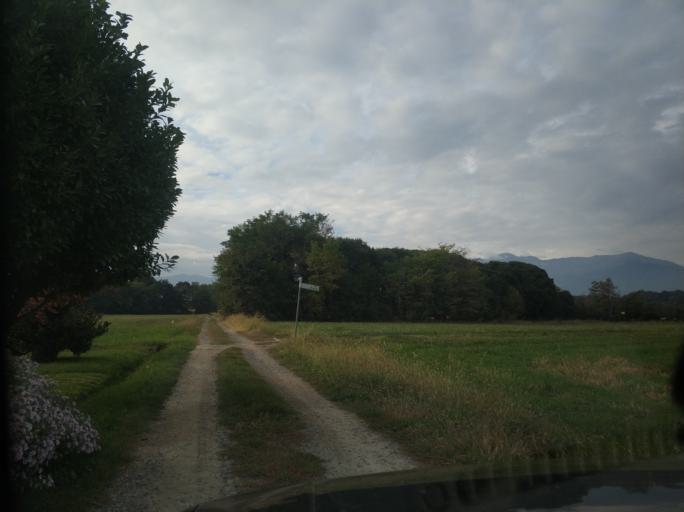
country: IT
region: Piedmont
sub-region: Provincia di Torino
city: Nole
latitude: 45.2499
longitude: 7.5681
